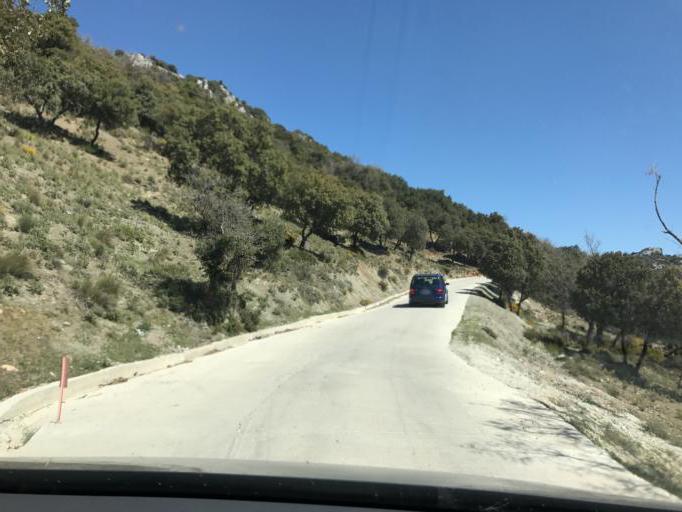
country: ES
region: Andalusia
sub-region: Provincia de Granada
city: Beas de Granada
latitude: 37.3117
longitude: -3.4619
